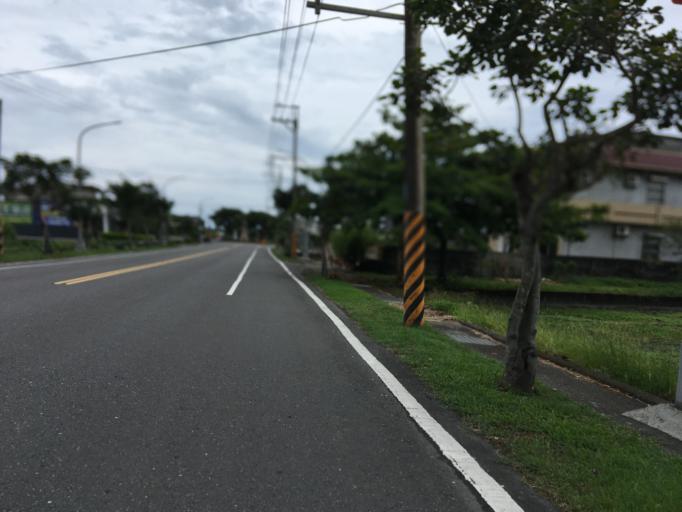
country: TW
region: Taiwan
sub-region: Yilan
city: Yilan
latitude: 24.6923
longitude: 121.8074
